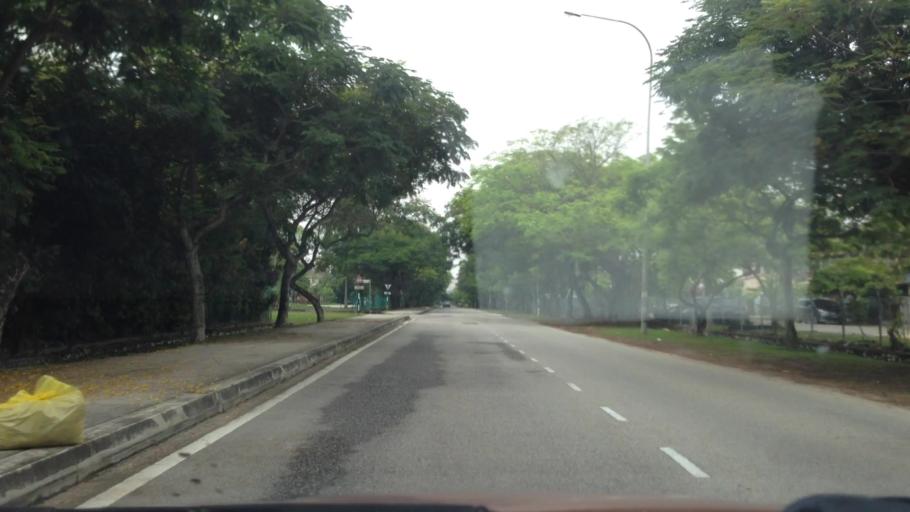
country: MY
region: Selangor
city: Subang Jaya
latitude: 3.0526
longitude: 101.5739
